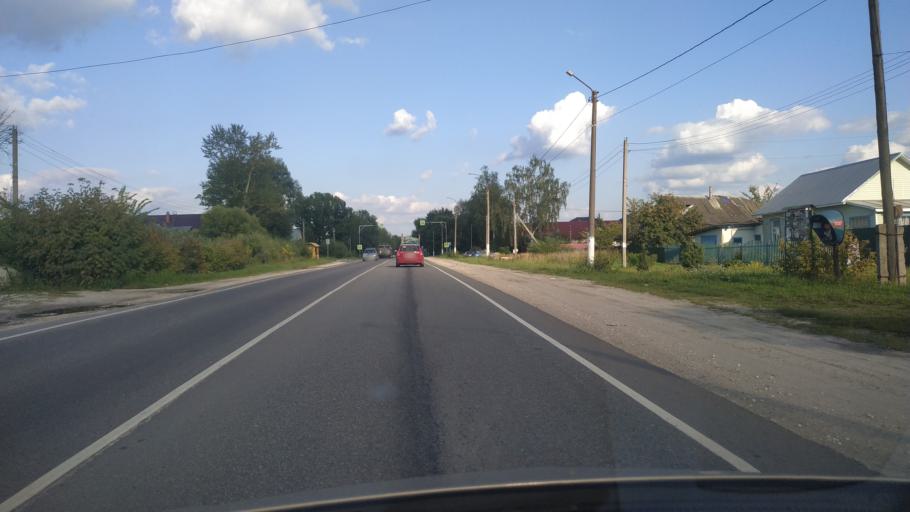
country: RU
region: Moskovskaya
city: Shaturtorf
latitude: 55.5794
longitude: 39.4756
